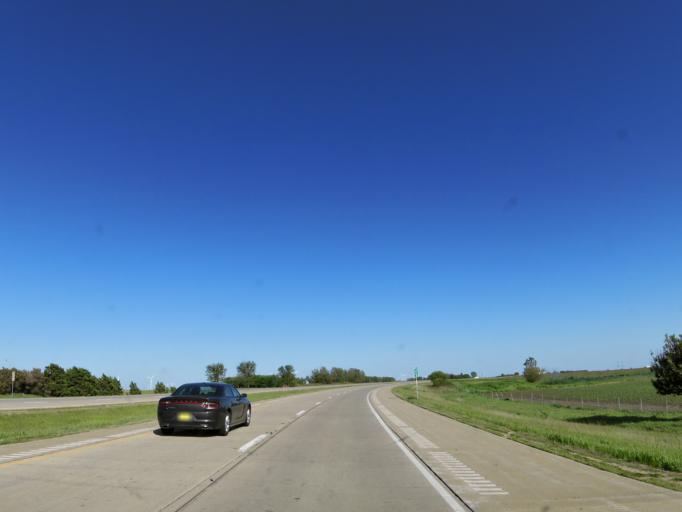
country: US
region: Illinois
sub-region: Woodford County
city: Minonk
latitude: 40.8915
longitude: -89.0424
